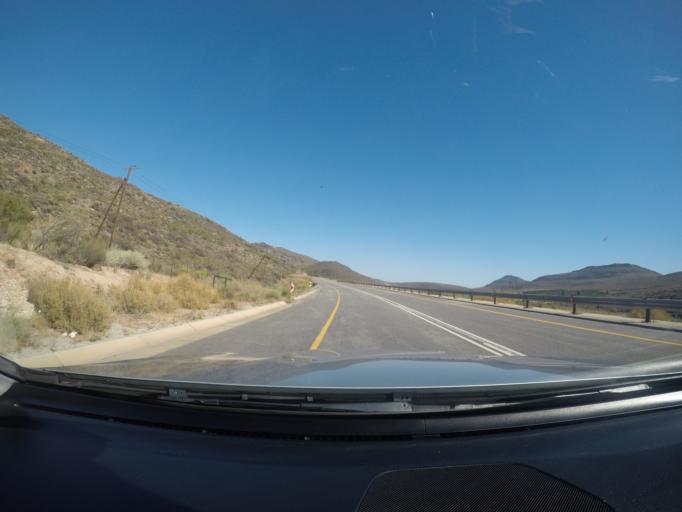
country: ZA
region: Western Cape
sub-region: West Coast District Municipality
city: Clanwilliam
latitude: -32.4017
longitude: 18.9543
